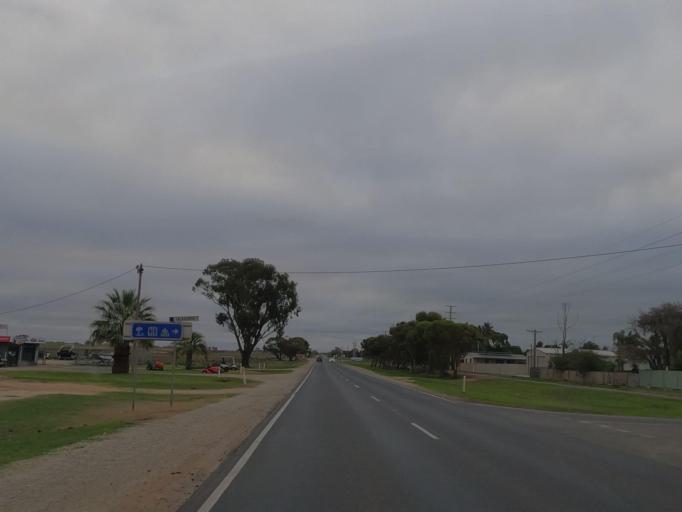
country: AU
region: Victoria
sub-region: Swan Hill
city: Swan Hill
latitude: -35.4539
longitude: 143.6272
